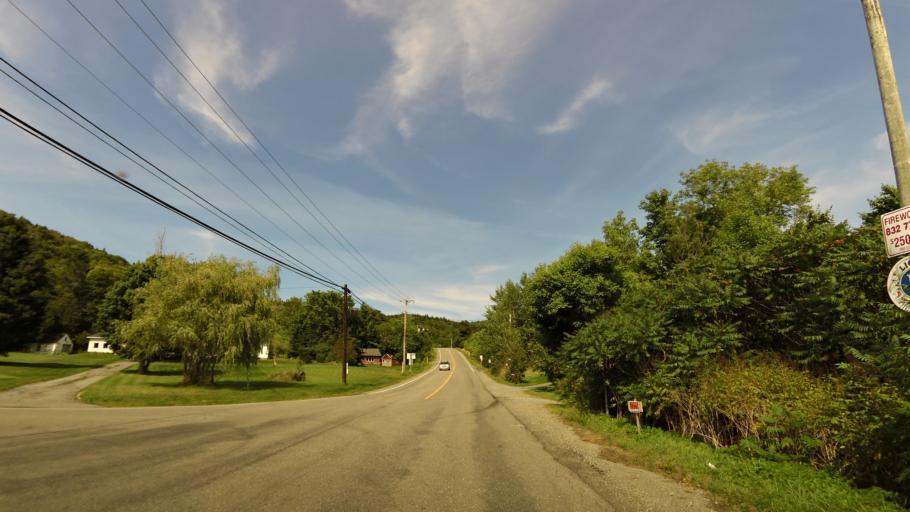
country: CA
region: New Brunswick
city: Hampton
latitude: 45.5461
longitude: -65.8363
